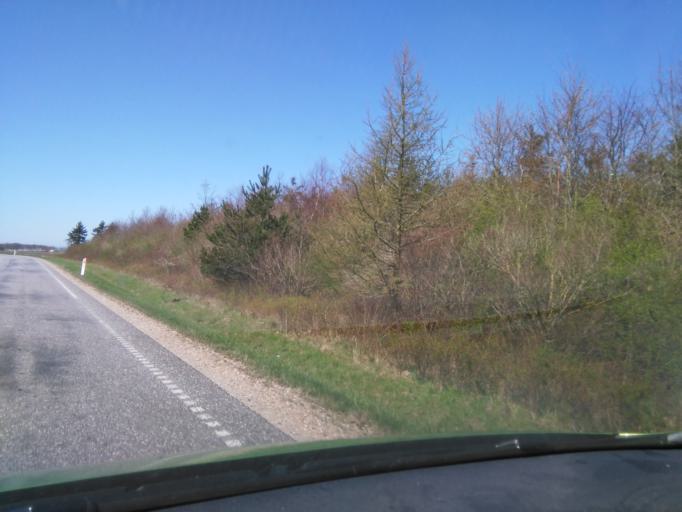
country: DK
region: South Denmark
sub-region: Billund Kommune
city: Grindsted
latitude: 55.7004
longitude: 8.8154
